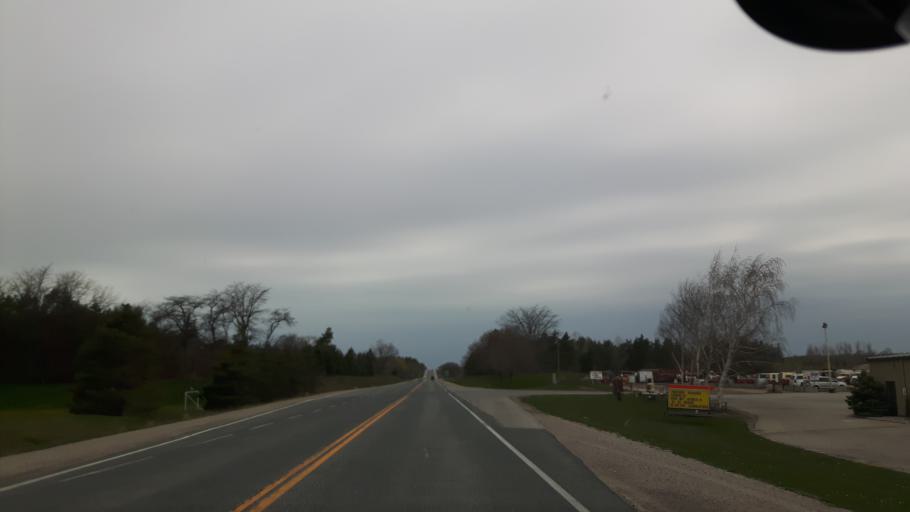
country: CA
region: Ontario
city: Goderich
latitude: 43.6432
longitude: -81.5962
